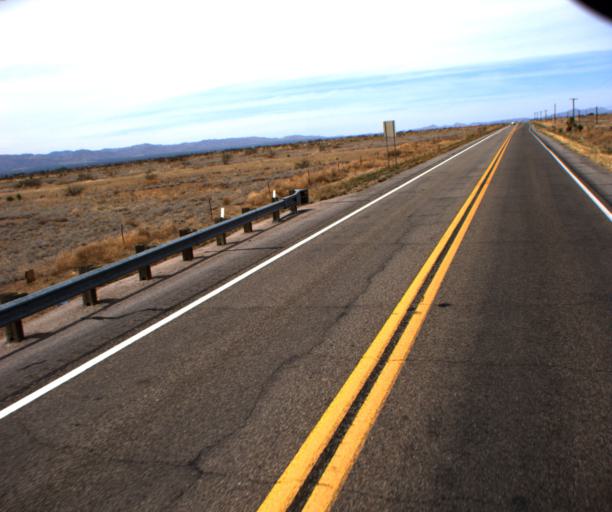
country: US
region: Arizona
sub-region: Cochise County
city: Pirtleville
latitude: 31.4479
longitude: -109.6027
